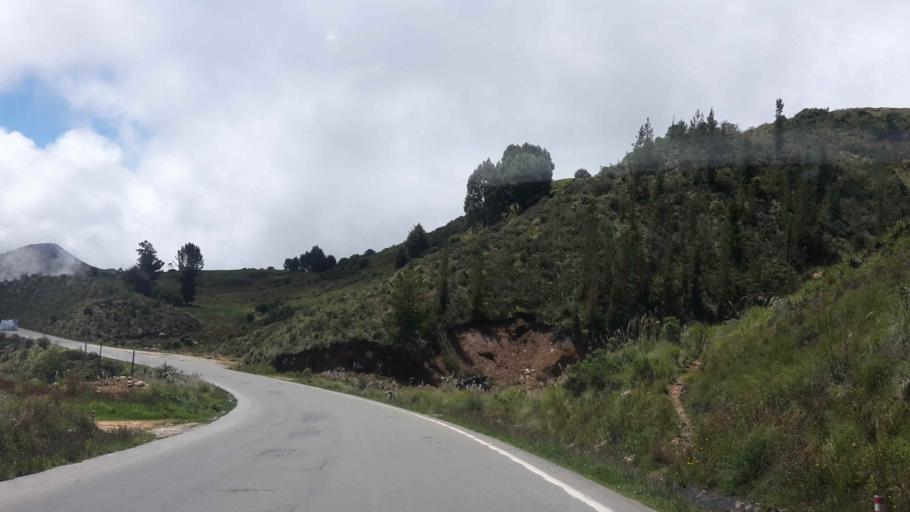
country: BO
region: Cochabamba
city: Colomi
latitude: -17.2563
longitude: -65.8920
